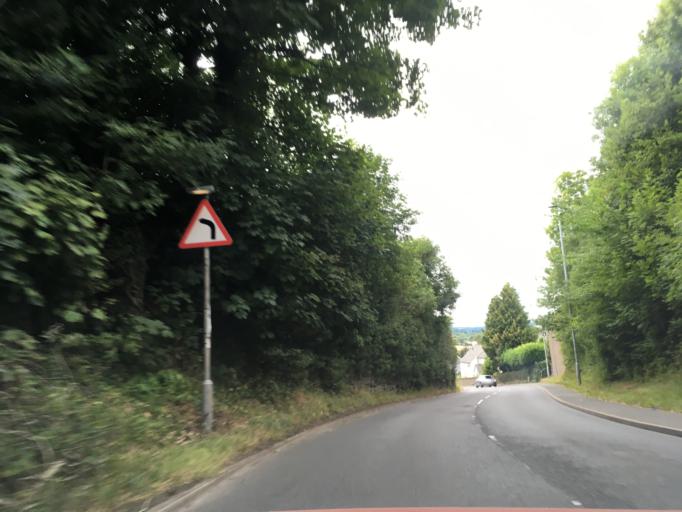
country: GB
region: Wales
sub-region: Blaenau Gwent
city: Brynmawr
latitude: 51.8913
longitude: -3.2402
